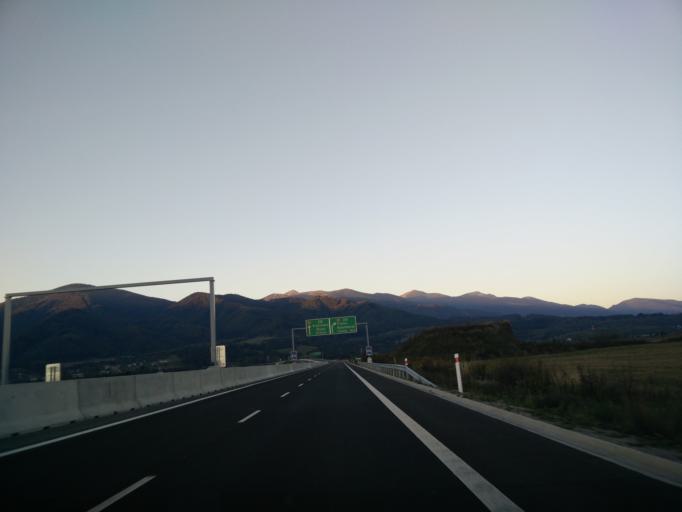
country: SK
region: Zilinsky
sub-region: Okres Zilina
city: Vrutky
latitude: 49.1009
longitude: 18.9538
